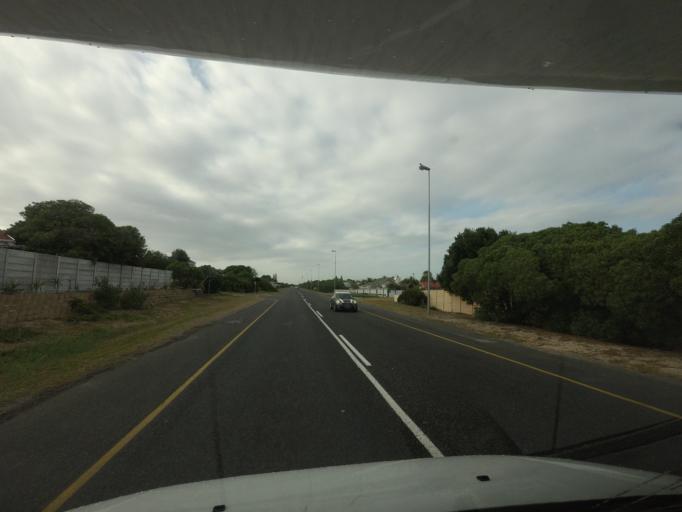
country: ZA
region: Western Cape
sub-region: City of Cape Town
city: Sunset Beach
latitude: -33.7193
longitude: 18.4462
